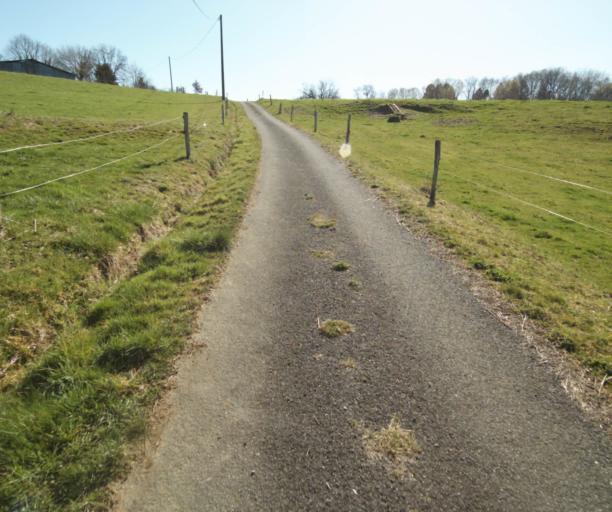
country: FR
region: Limousin
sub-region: Departement de la Correze
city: Chamboulive
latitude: 45.4224
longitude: 1.6670
